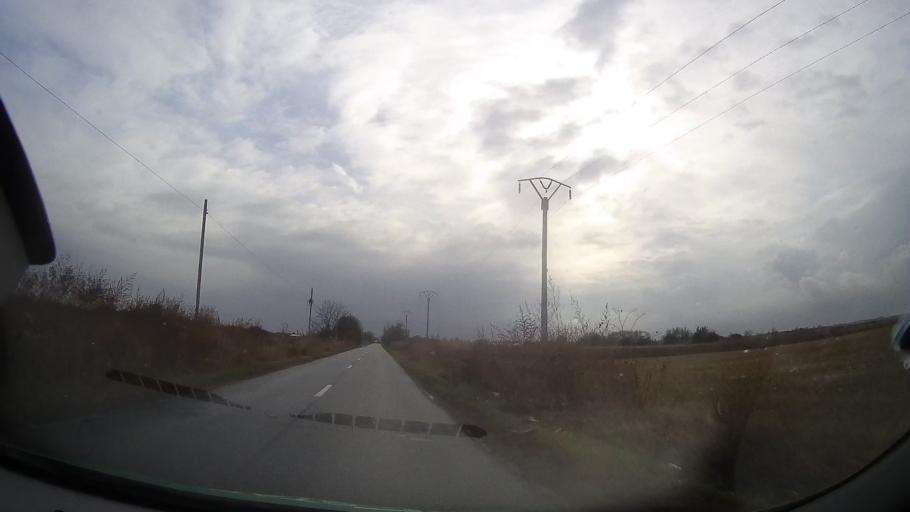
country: RO
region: Ialomita
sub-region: Comuna Fierbinti-Targ
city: Fierbintii de Jos
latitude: 44.7044
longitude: 26.3928
